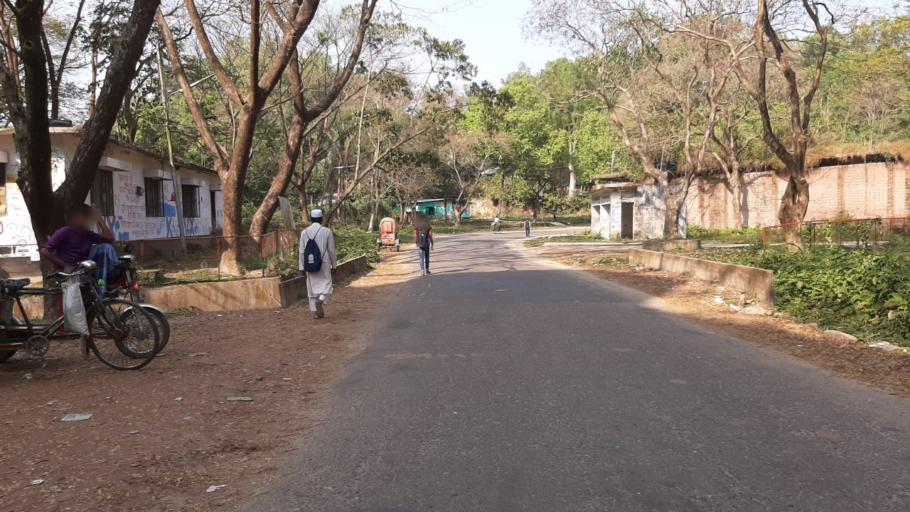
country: BD
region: Chittagong
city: Chittagong
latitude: 22.4738
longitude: 91.7884
